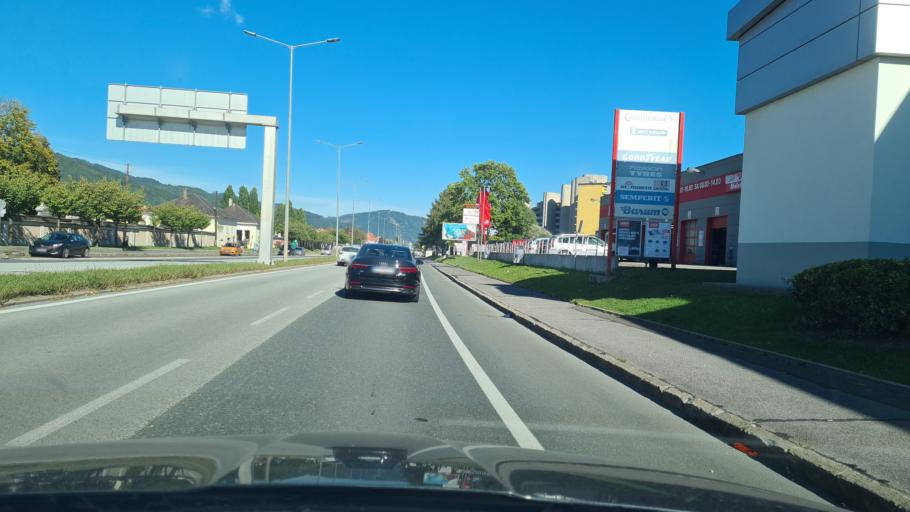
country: AT
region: Styria
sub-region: Politischer Bezirk Leoben
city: Leoben
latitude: 47.3815
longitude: 15.1080
